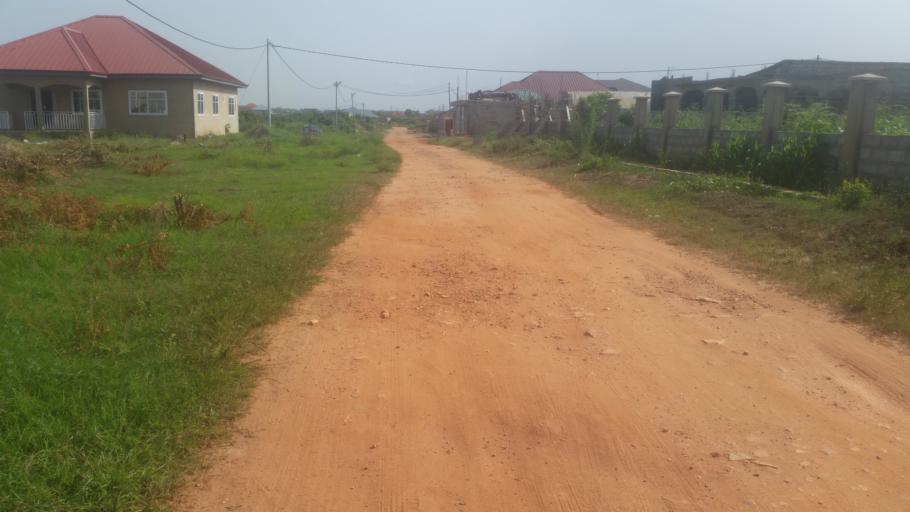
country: GH
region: Greater Accra
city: Tema
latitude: 5.7594
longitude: 0.0717
